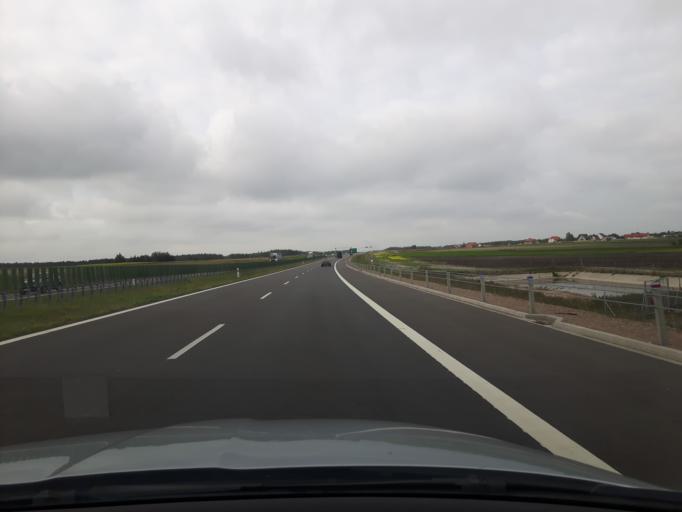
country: PL
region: Swietokrzyskie
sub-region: Powiat jedrzejowski
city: Sobkow
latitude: 50.6944
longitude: 20.3853
